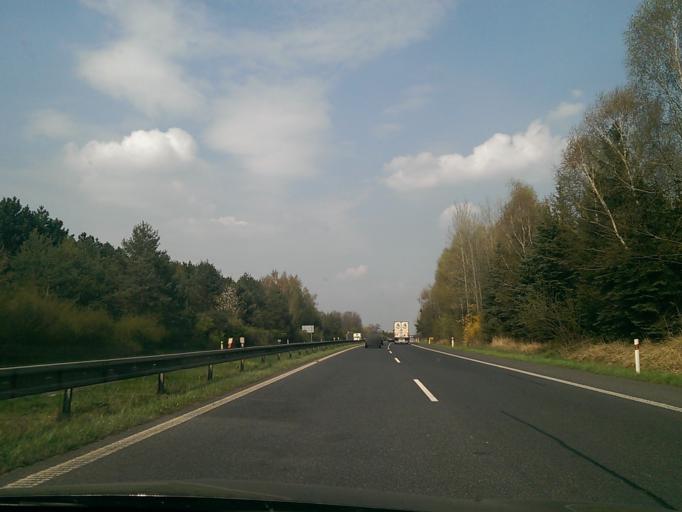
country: CZ
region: Central Bohemia
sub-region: Okres Mlada Boleslav
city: Mlada Boleslav
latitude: 50.3606
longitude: 14.8747
